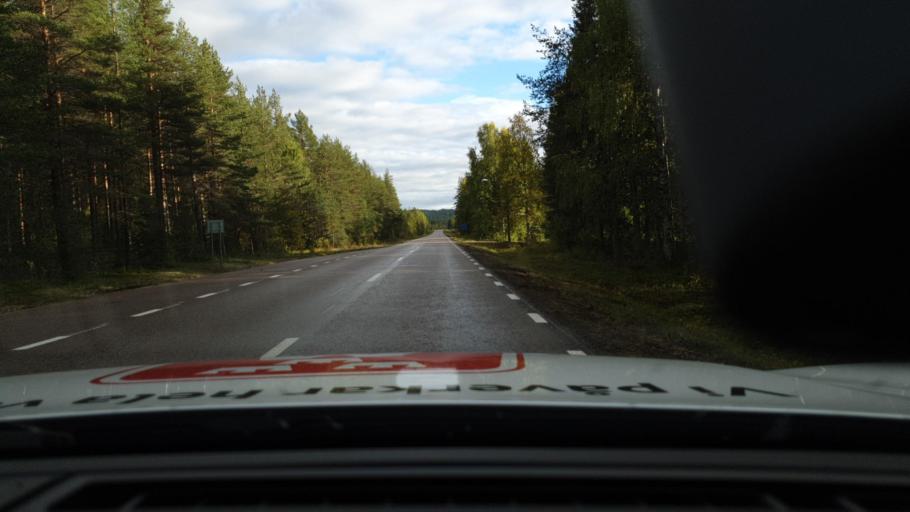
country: SE
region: Norrbotten
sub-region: Overkalix Kommun
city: OEverkalix
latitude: 66.6176
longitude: 22.7508
